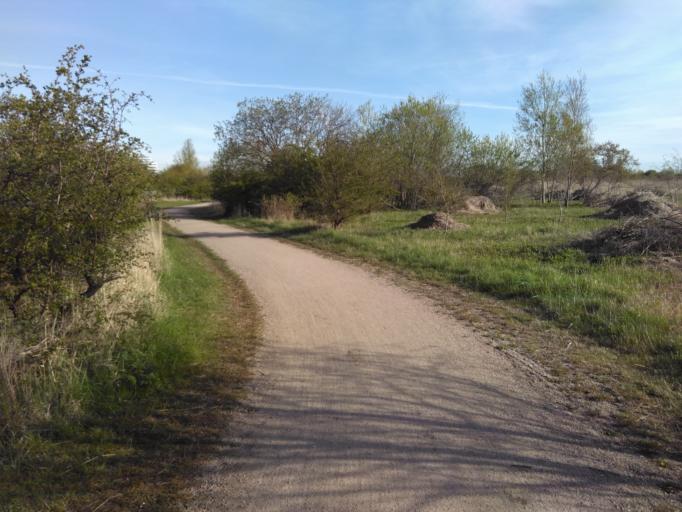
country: DK
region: Capital Region
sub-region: Kobenhavn
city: Copenhagen
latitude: 55.6480
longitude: 12.5701
